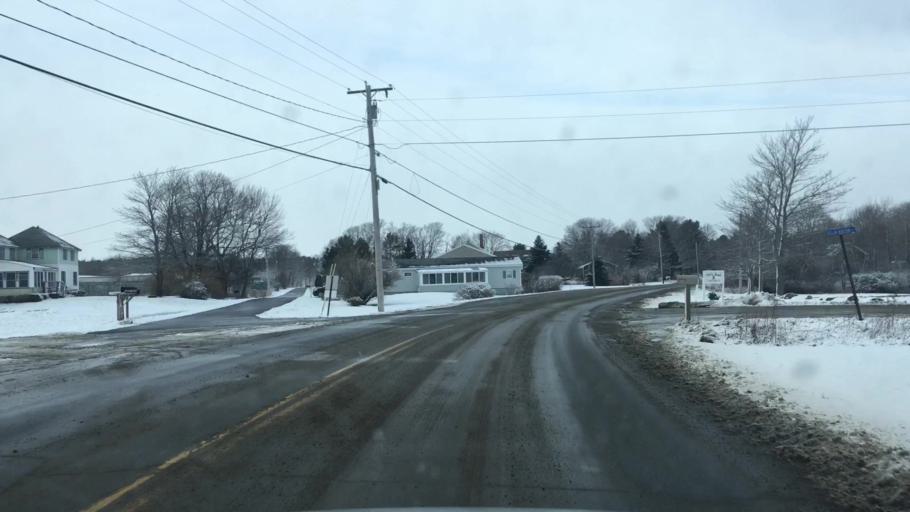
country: US
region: Maine
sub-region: Knox County
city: South Thomaston
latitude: 44.0626
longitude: -69.0927
